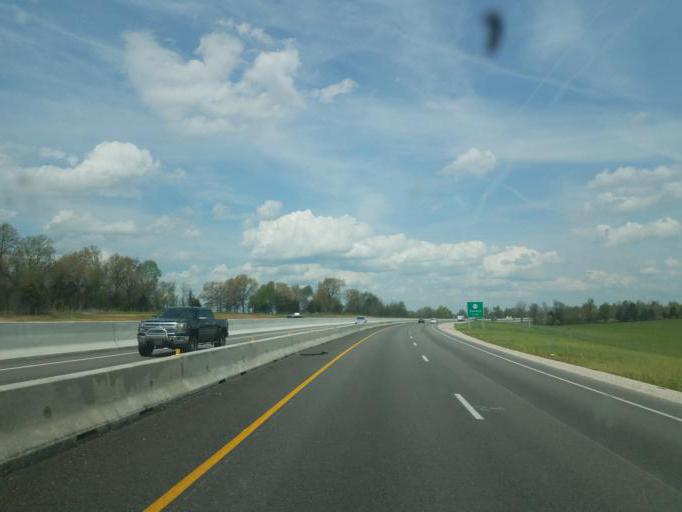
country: US
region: Kentucky
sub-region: Larue County
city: Hodgenville
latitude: 37.5013
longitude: -85.8873
